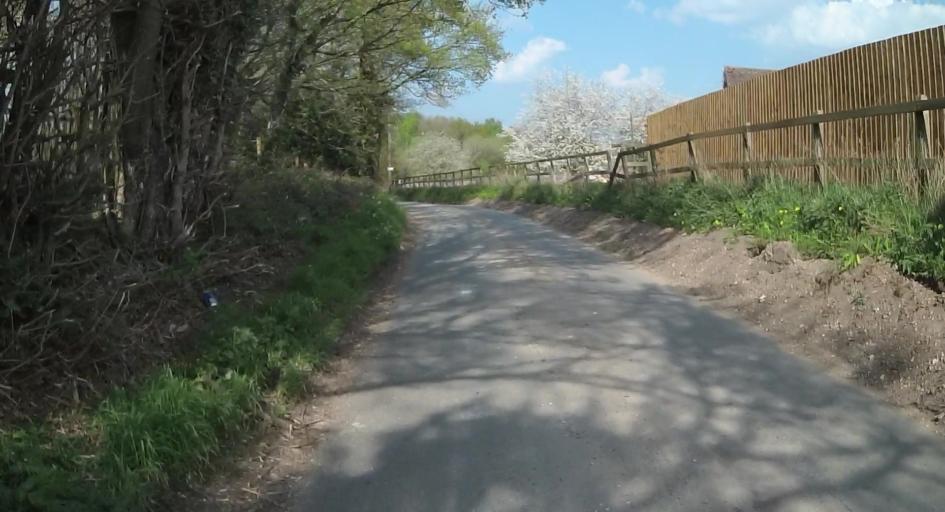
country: GB
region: England
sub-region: Hampshire
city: Tadley
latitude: 51.3876
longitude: -1.1277
